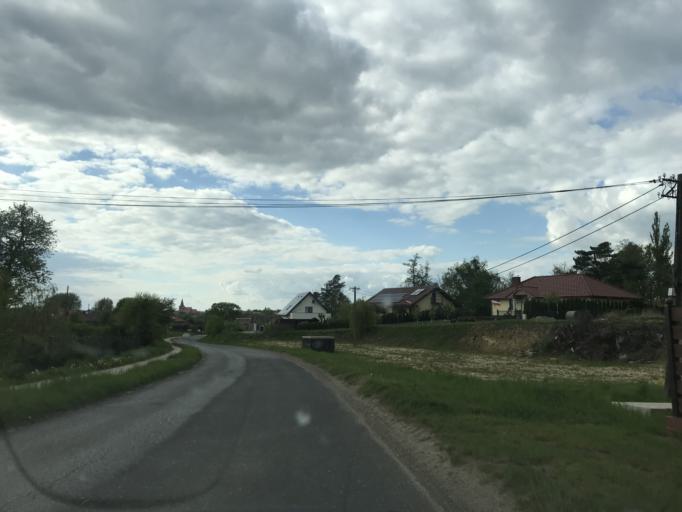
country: PL
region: West Pomeranian Voivodeship
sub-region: Powiat mysliborski
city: Mysliborz
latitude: 52.9163
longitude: 14.8891
